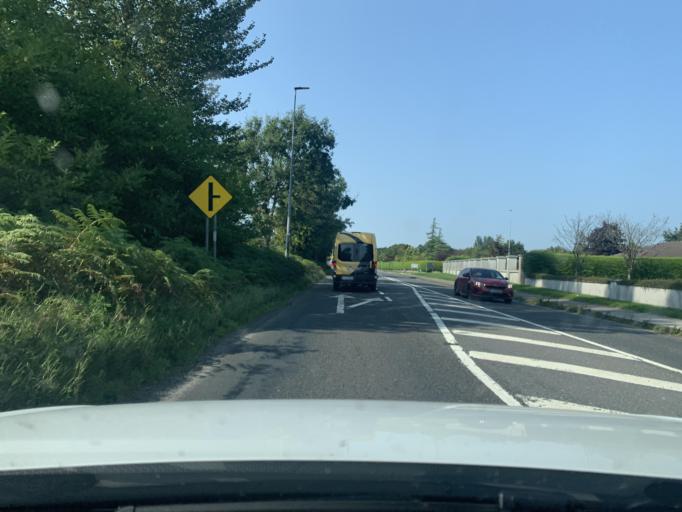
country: IE
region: Leinster
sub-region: An Iarmhi
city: Athlone
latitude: 53.4542
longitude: -7.9927
